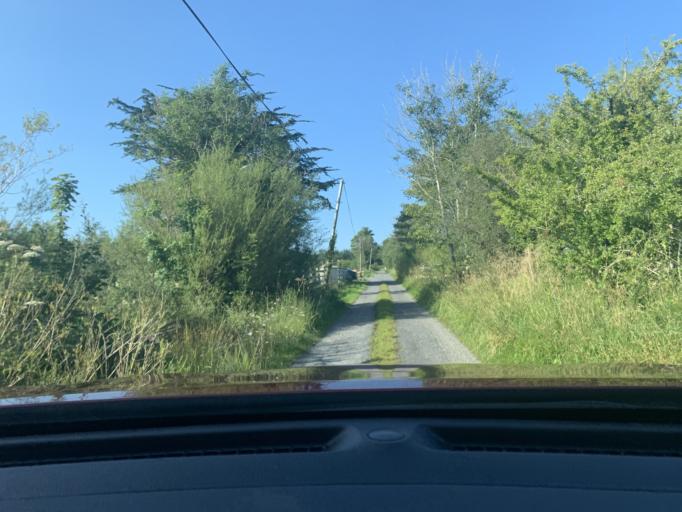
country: IE
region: Connaught
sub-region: Sligo
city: Tobercurry
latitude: 54.0577
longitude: -8.7937
